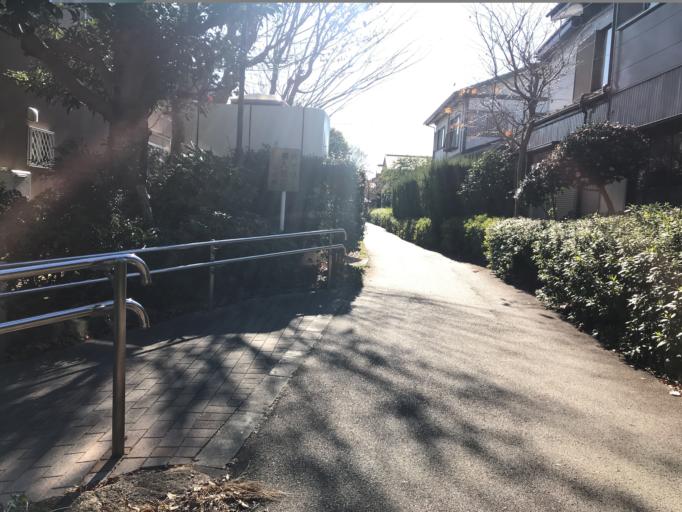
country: JP
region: Tokyo
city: Kokubunji
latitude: 35.7057
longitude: 139.4324
